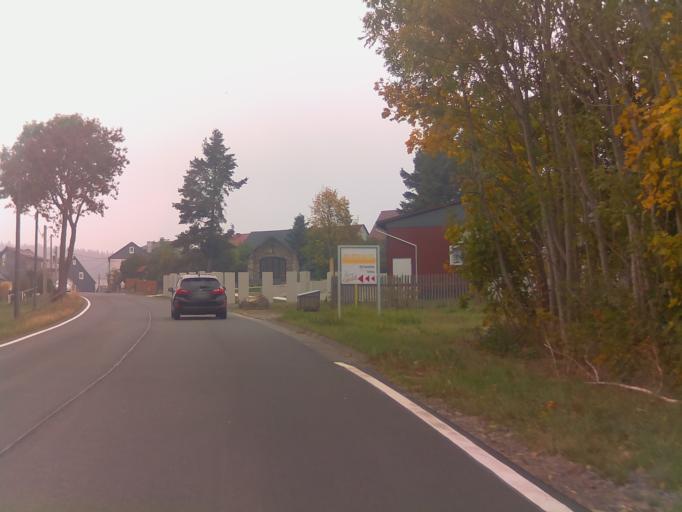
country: DE
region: Thuringia
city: Herschdorf
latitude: 50.6265
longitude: 11.0534
